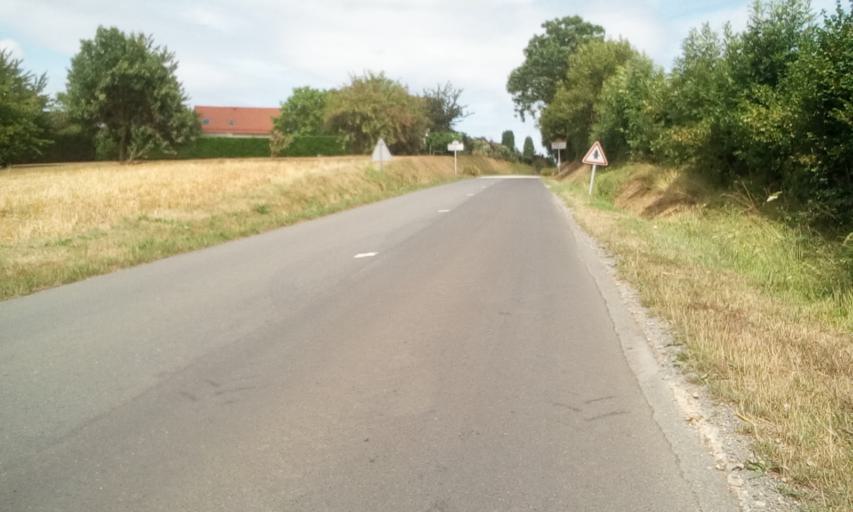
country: FR
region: Lower Normandy
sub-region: Departement du Calvados
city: Amfreville
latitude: 49.2388
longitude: -0.2280
